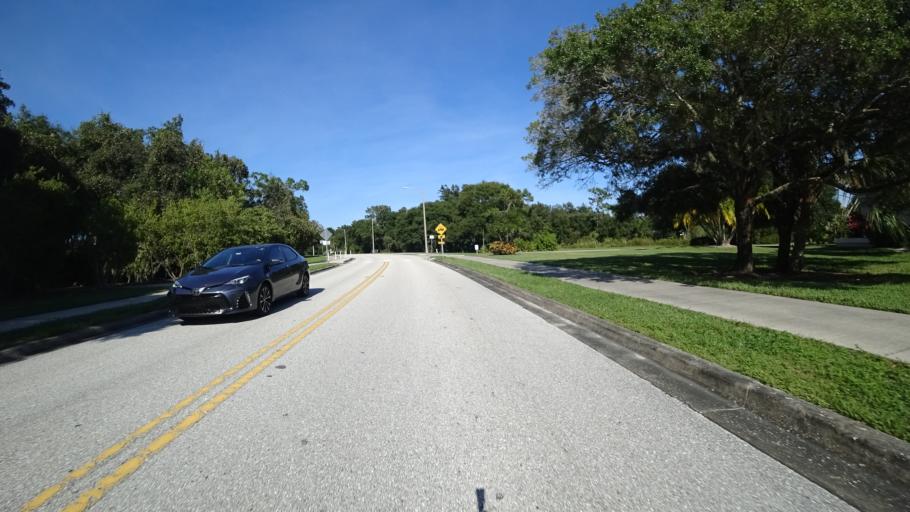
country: US
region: Florida
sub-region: Sarasota County
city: The Meadows
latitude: 27.4202
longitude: -82.4334
